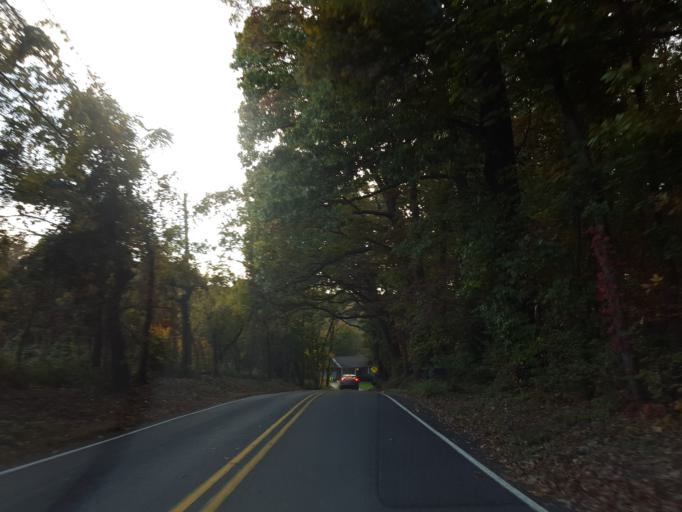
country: US
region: Pennsylvania
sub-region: York County
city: Spry
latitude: 39.9233
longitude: -76.6726
